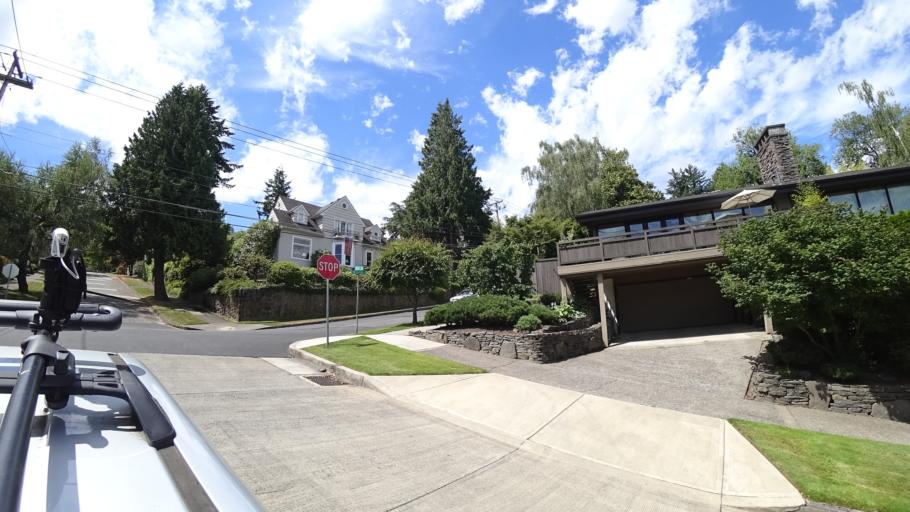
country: US
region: Oregon
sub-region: Multnomah County
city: Portland
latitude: 45.5116
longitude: -122.6958
